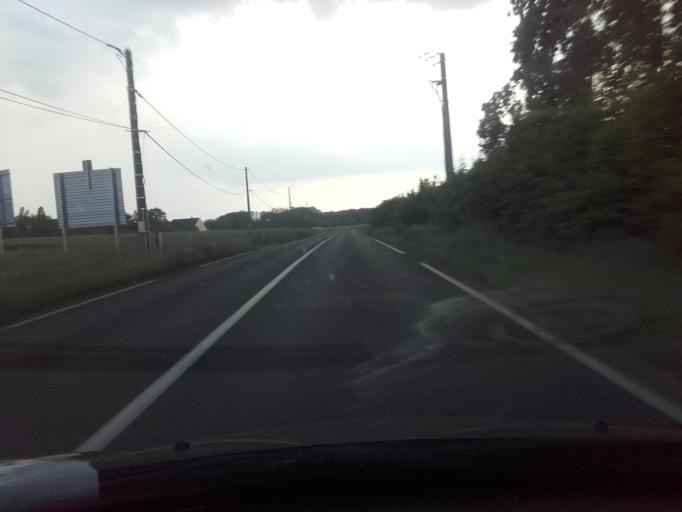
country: FR
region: Centre
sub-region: Departement d'Indre-et-Loire
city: Auzouer-en-Touraine
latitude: 47.5357
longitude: 0.9868
